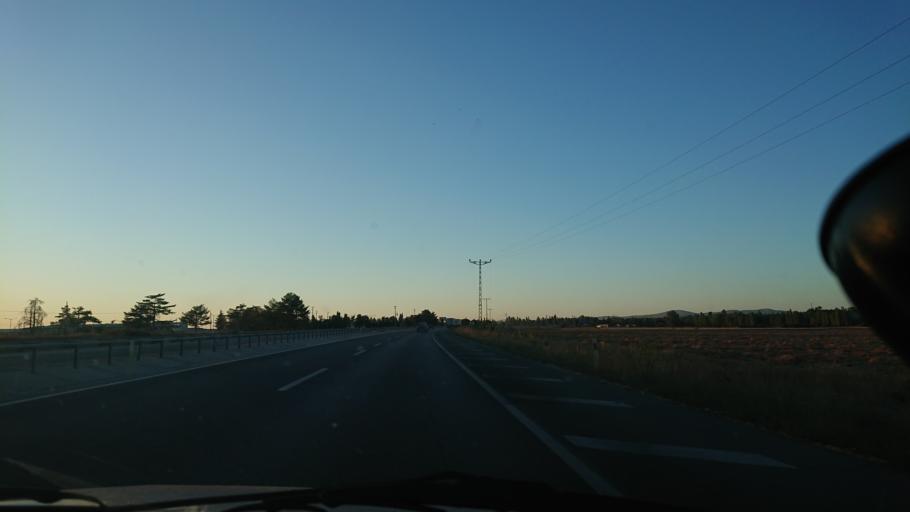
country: TR
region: Eskisehir
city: Mahmudiye
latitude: 39.5584
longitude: 30.9184
